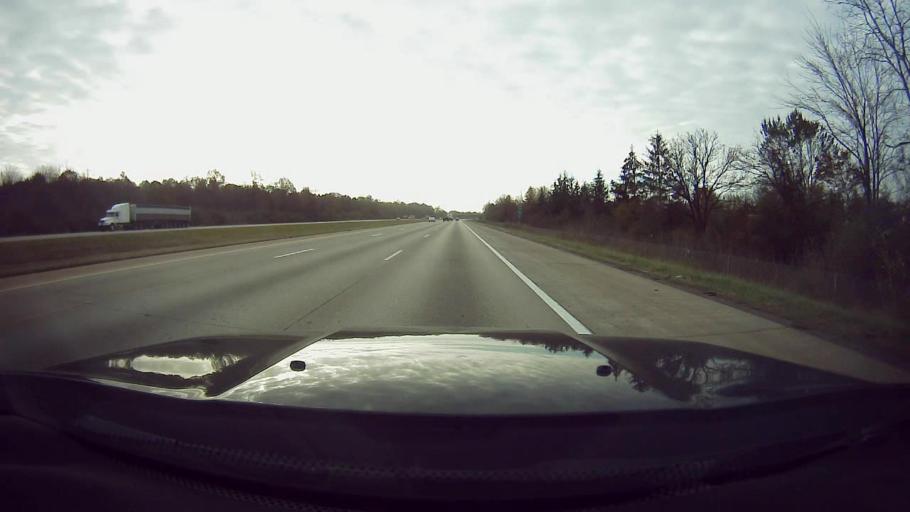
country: US
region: Michigan
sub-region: Monroe County
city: Carleton
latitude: 42.1225
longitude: -83.3801
